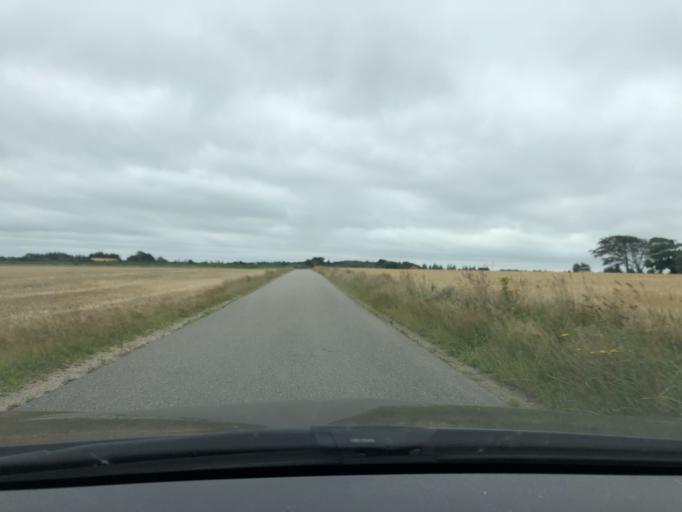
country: DK
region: South Denmark
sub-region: Varde Kommune
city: Olgod
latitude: 55.8030
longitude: 8.5813
